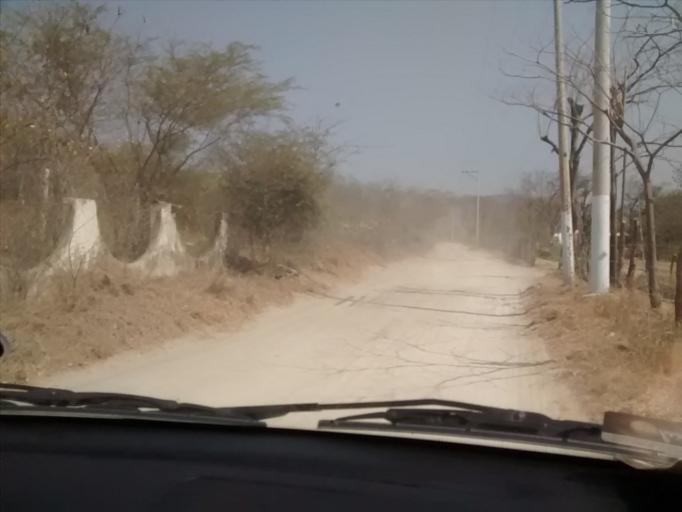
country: CO
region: Magdalena
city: Santa Marta
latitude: 11.1648
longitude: -74.2156
